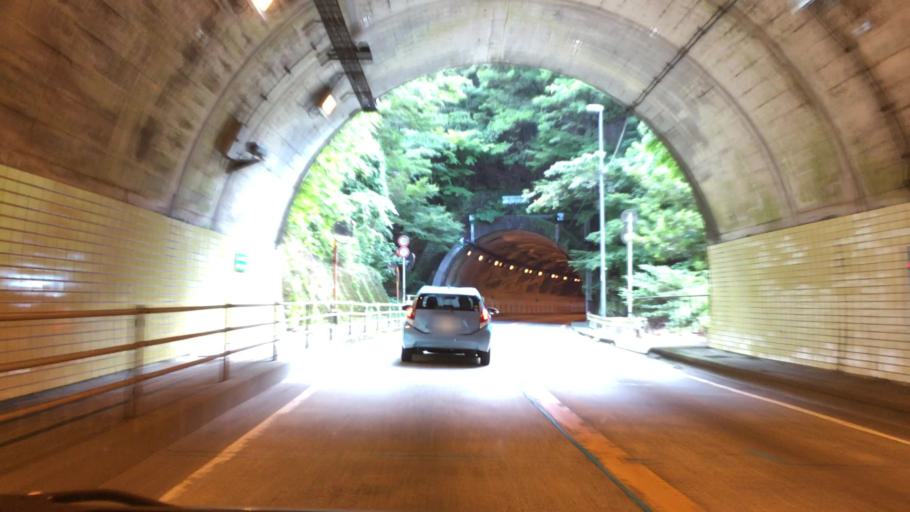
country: JP
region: Saga Prefecture
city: Imaricho-ko
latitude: 33.1882
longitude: 129.8995
